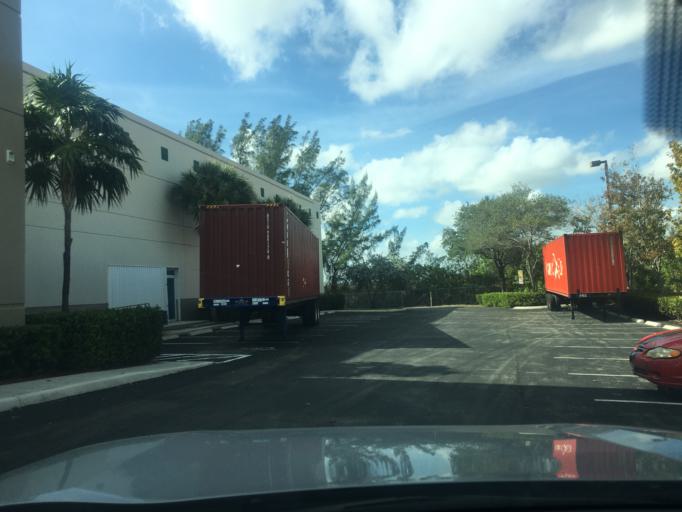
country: US
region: Florida
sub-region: Broward County
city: Broadview Park
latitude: 26.0769
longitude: -80.1841
